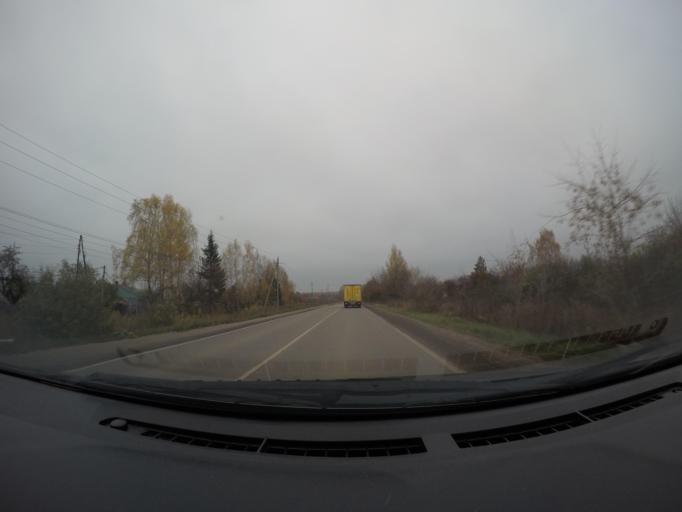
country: RU
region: Moskovskaya
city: Rechitsy
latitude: 55.5993
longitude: 38.4343
